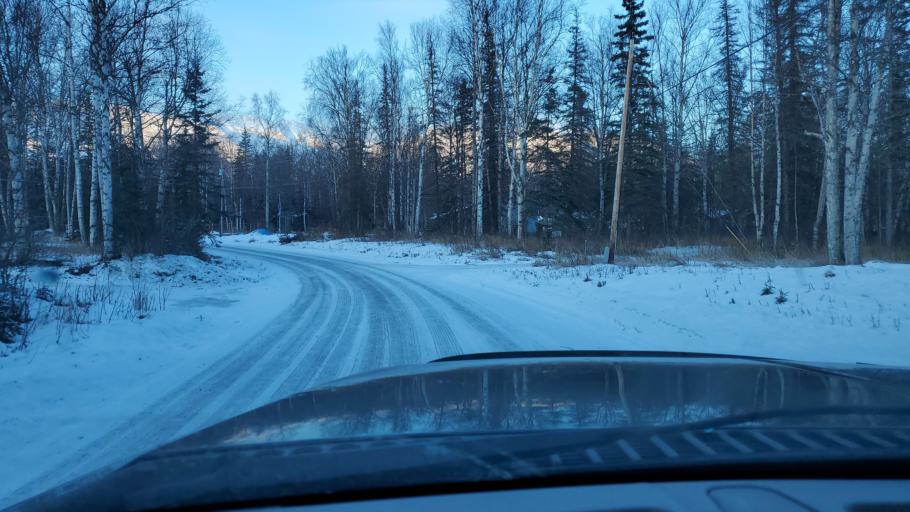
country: US
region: Alaska
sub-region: Matanuska-Susitna Borough
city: Lakes
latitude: 61.6672
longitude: -149.2939
